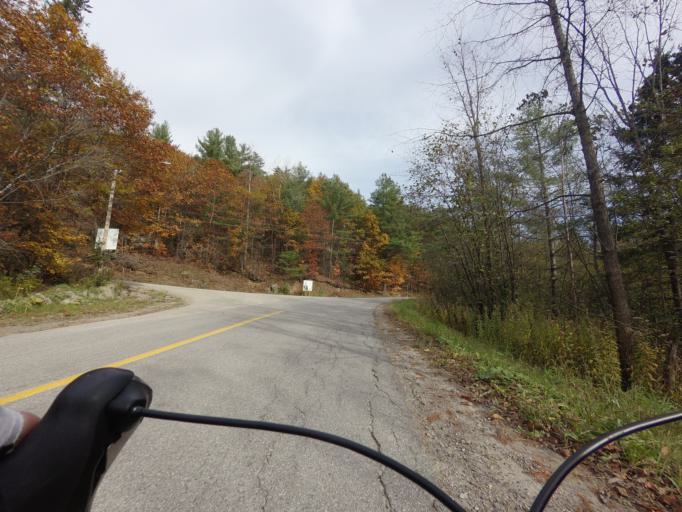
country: CA
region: Quebec
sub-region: Outaouais
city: Val-des-Monts
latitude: 45.5809
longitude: -75.6409
